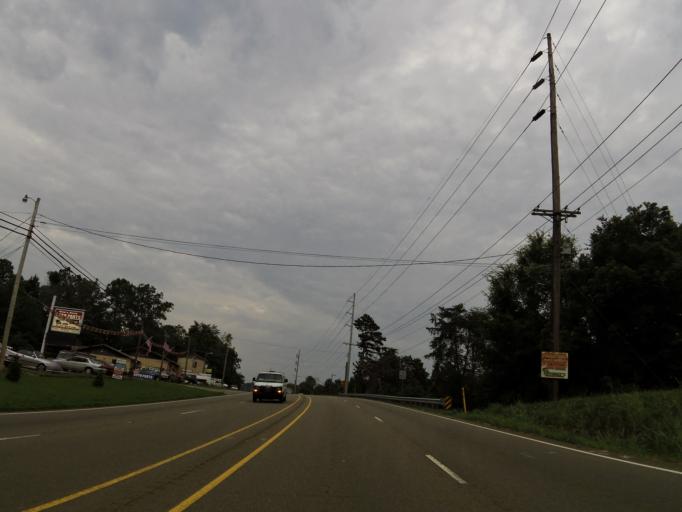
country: US
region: Tennessee
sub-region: Sevier County
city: Seymour
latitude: 35.9017
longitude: -83.8257
